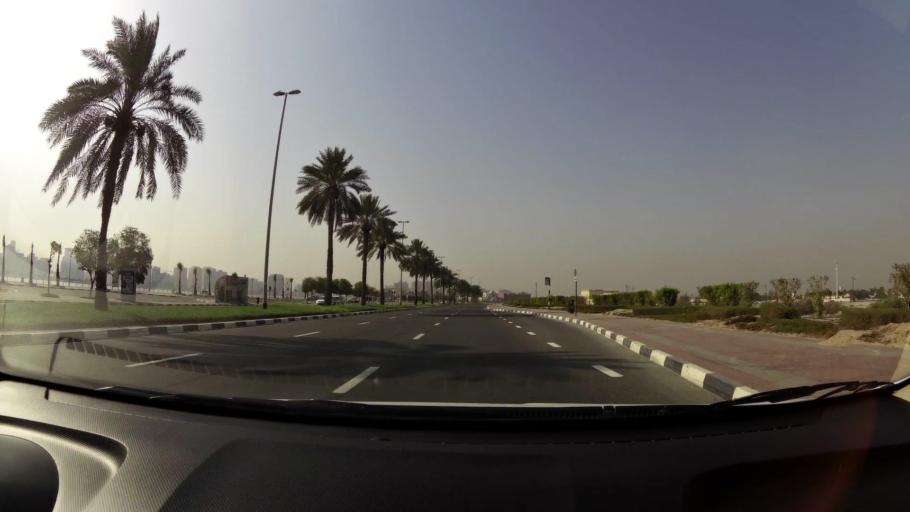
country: AE
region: Ash Shariqah
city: Sharjah
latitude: 25.3026
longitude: 55.3483
